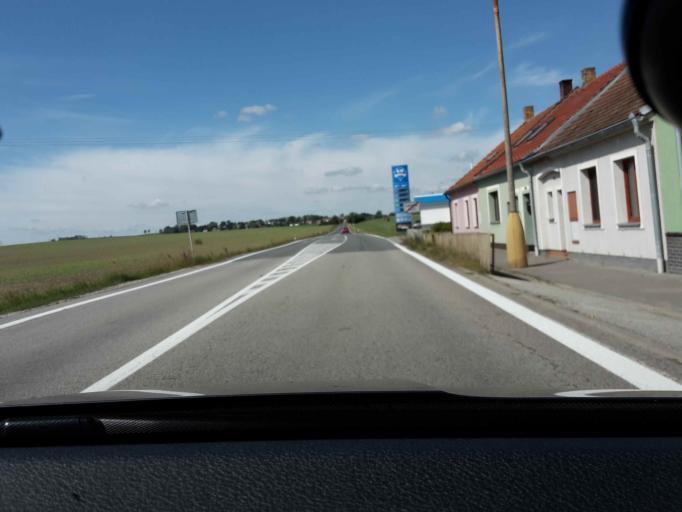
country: CZ
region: Jihocesky
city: Kardasova Recice
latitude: 49.1871
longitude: 14.8463
